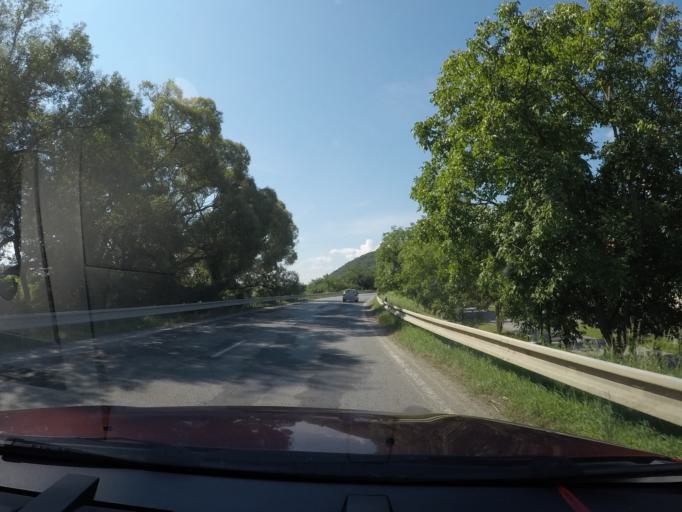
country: SK
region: Presovsky
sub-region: Okres Presov
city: Presov
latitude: 48.9516
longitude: 21.2415
